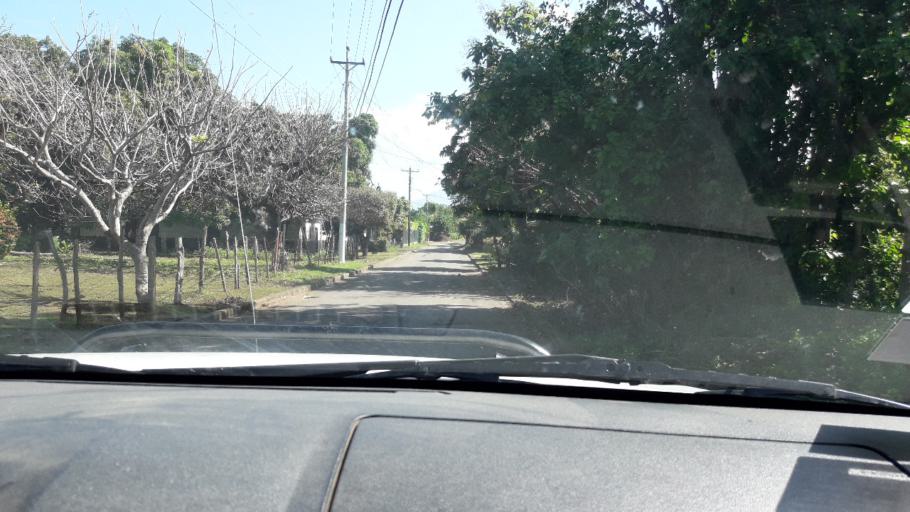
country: NI
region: Rivas
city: Rivas
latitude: 11.4546
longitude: -85.8288
